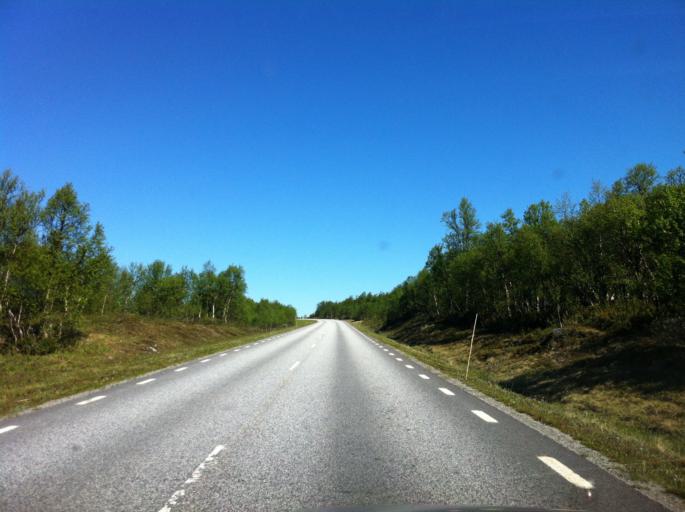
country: NO
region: Sor-Trondelag
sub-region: Tydal
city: Aas
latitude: 62.6158
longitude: 12.1391
